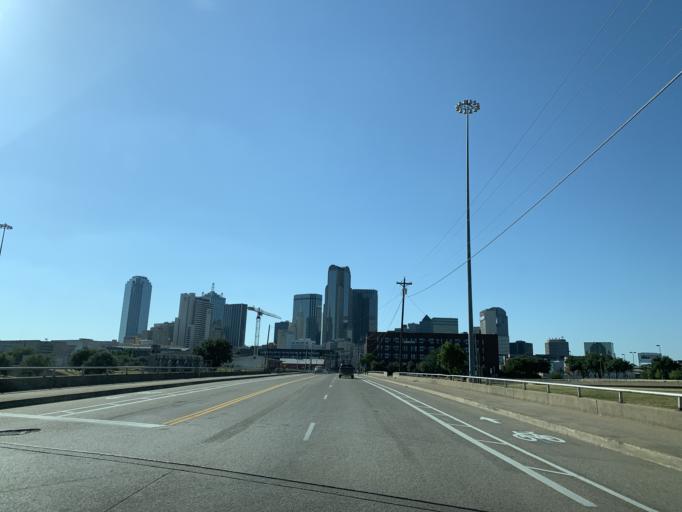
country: US
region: Texas
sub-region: Dallas County
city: Dallas
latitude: 32.7743
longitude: -96.7869
